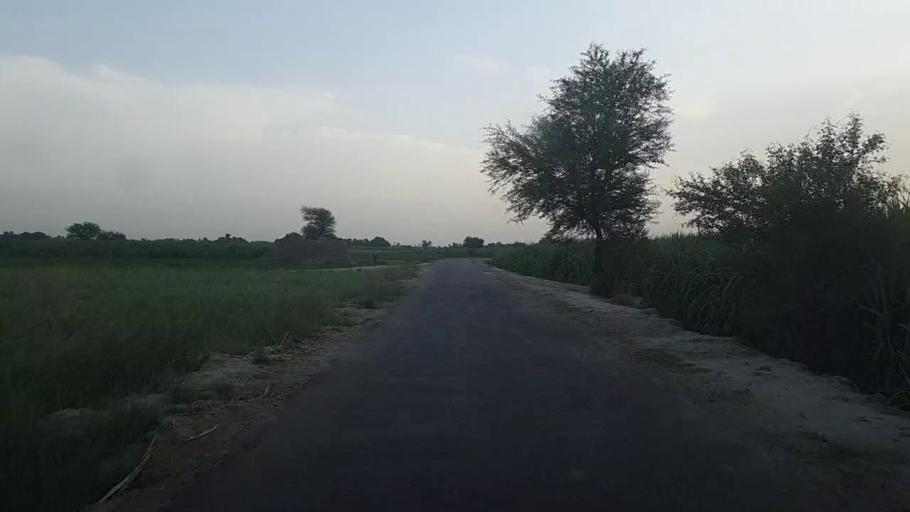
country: PK
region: Sindh
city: Ubauro
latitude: 28.3559
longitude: 69.7836
